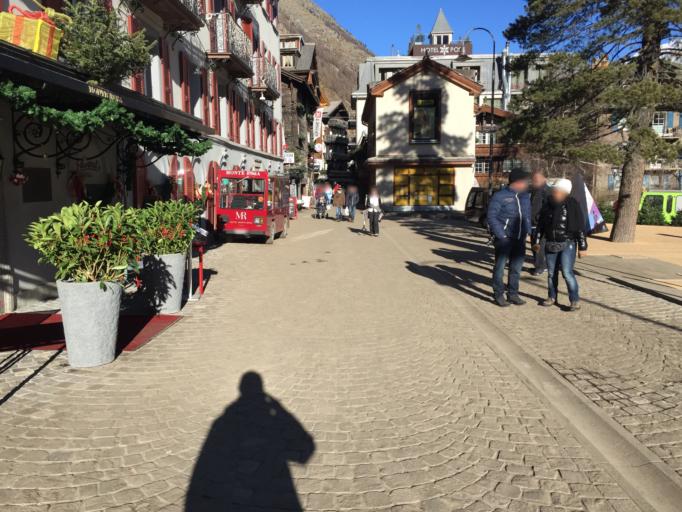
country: CH
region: Valais
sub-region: Visp District
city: Zermatt
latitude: 46.0201
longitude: 7.7462
